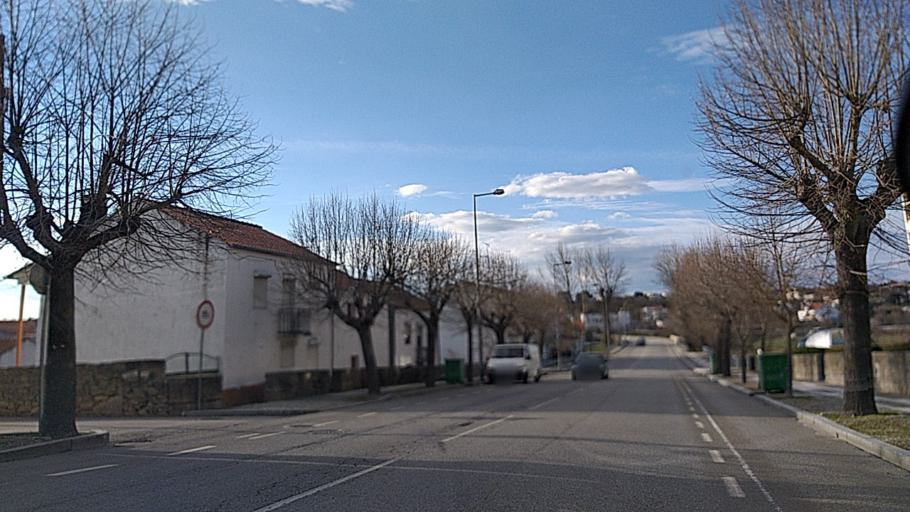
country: ES
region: Castille and Leon
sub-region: Provincia de Salamanca
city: Fuentes de Onoro
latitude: 40.6123
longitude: -6.8326
